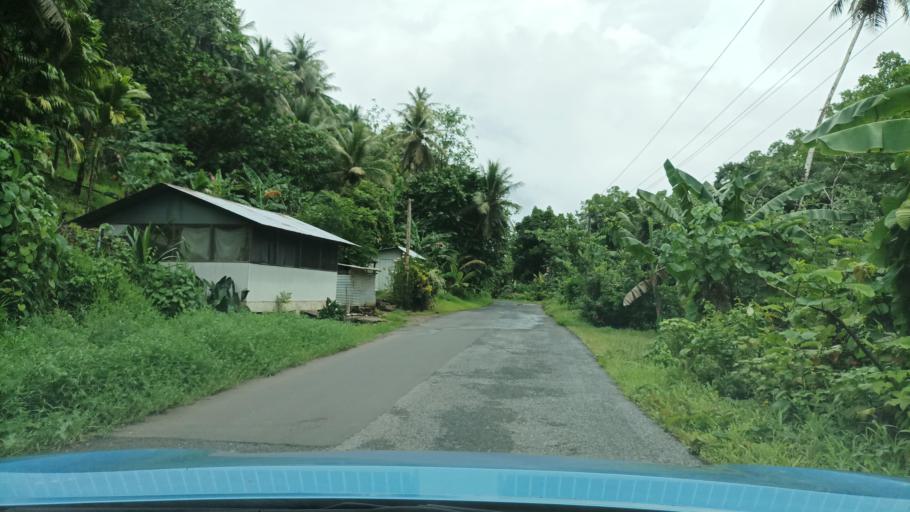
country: FM
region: Pohnpei
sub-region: Madolenihm Municipality
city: Madolenihm Municipality Government
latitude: 6.9091
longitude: 158.3224
